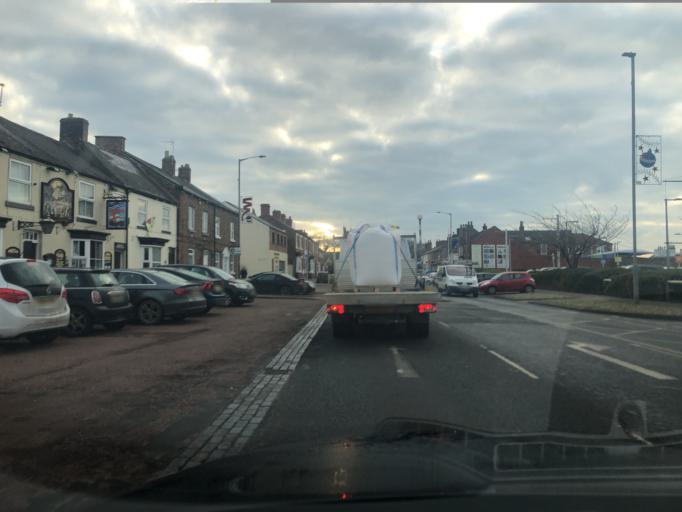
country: GB
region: England
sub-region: North Yorkshire
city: Northallerton
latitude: 54.3447
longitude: -1.4385
